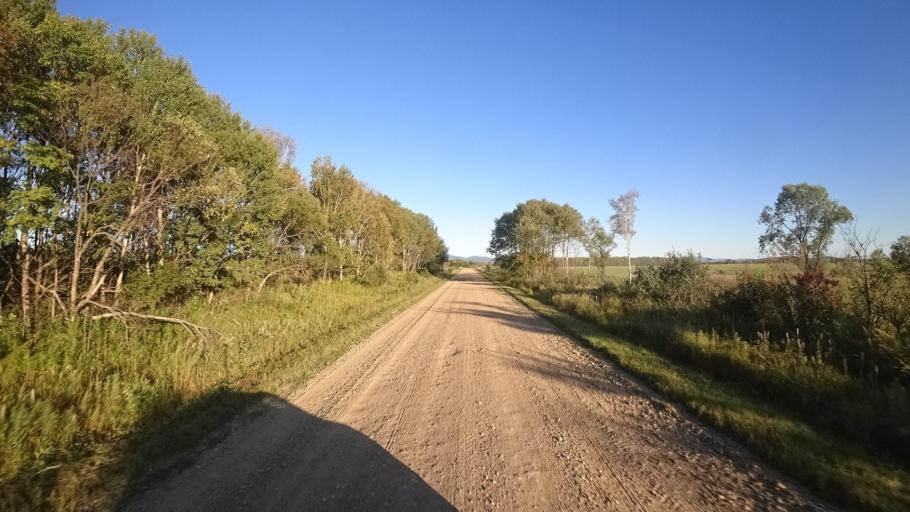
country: RU
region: Primorskiy
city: Kirovskiy
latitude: 44.8245
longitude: 133.5994
